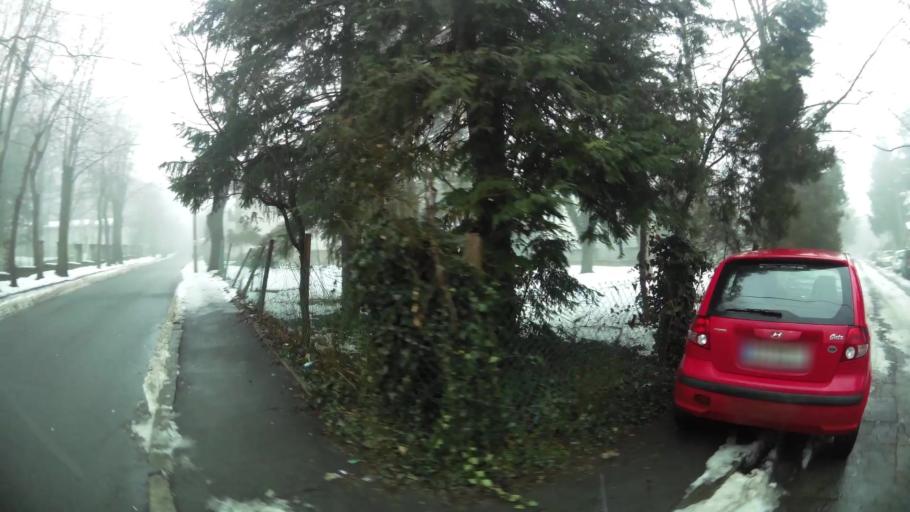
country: RS
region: Central Serbia
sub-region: Belgrade
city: Savski Venac
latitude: 44.7725
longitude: 20.4610
